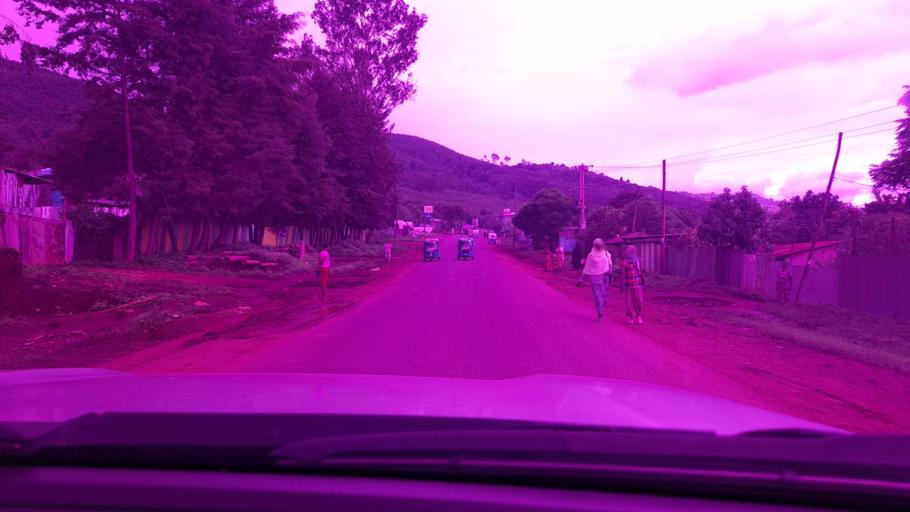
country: ET
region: Oromiya
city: Jima
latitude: 7.6697
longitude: 36.8680
